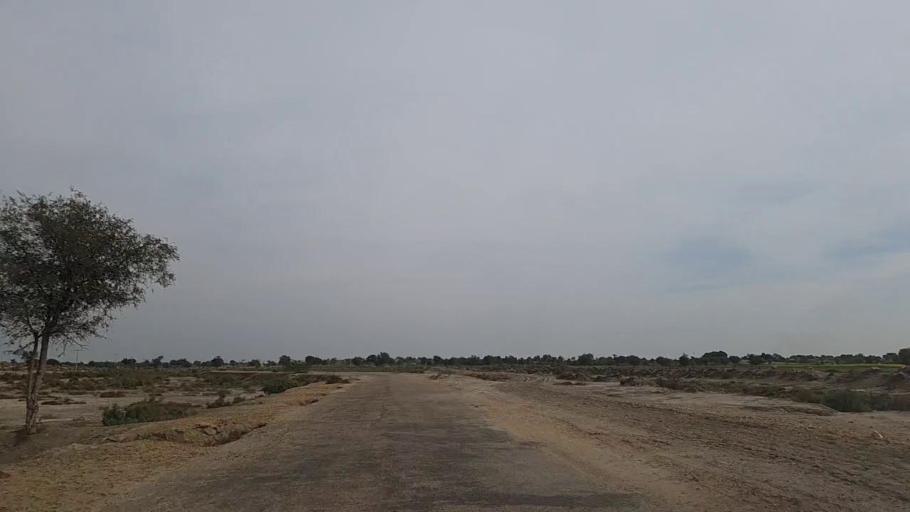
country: PK
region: Sindh
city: Jam Sahib
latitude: 26.3999
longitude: 68.5104
